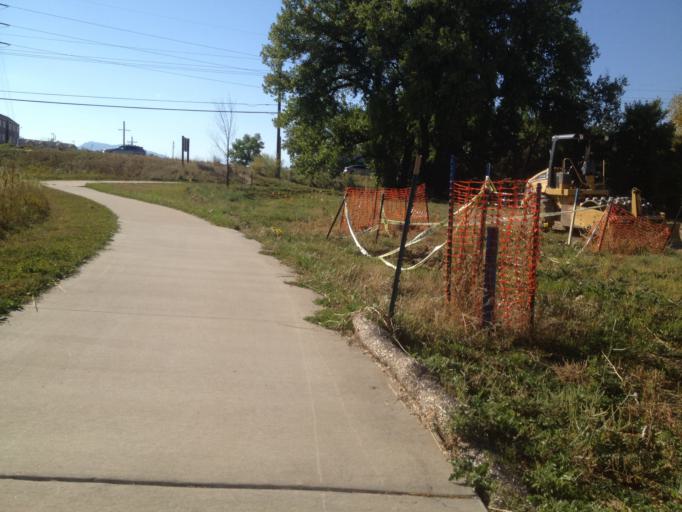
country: US
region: Colorado
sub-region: Boulder County
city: Louisville
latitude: 39.9908
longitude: -105.1269
